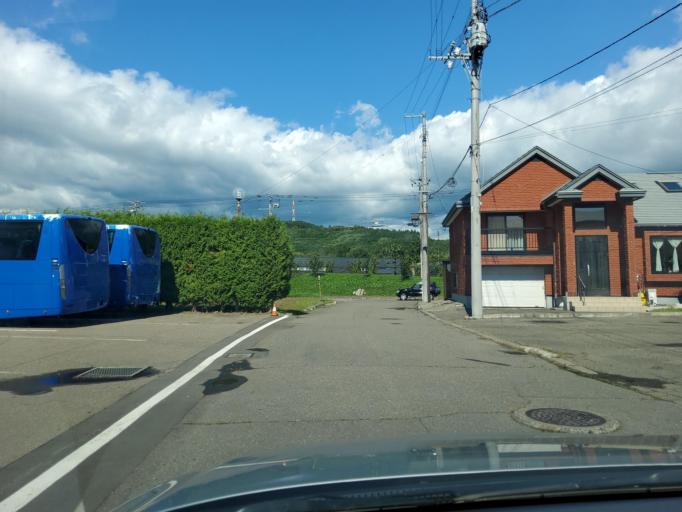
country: JP
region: Hokkaido
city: Obihiro
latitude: 42.9323
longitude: 143.3003
